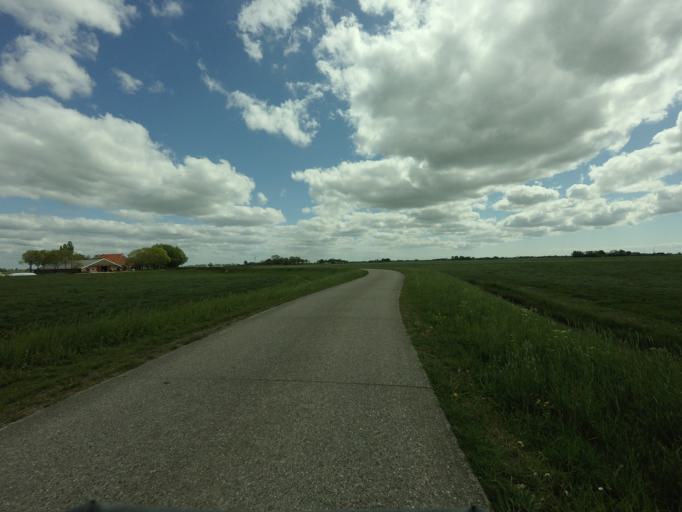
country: NL
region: Friesland
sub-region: Gemeente Littenseradiel
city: Wommels
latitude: 53.1147
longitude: 5.5501
